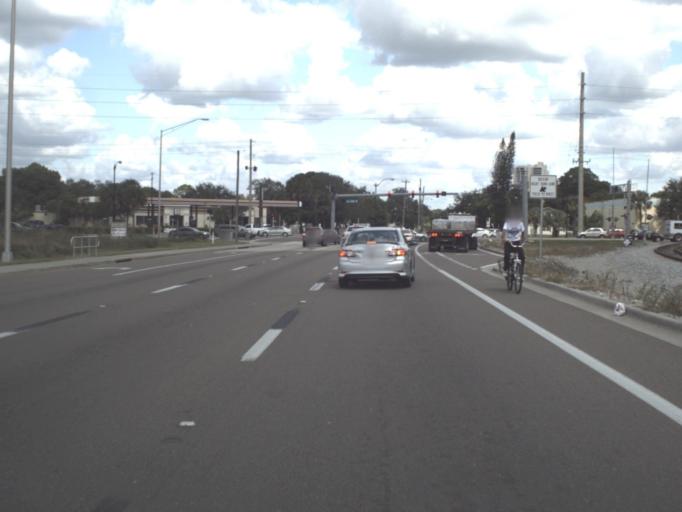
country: US
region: Florida
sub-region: Lee County
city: Fort Myers
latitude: 26.6399
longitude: -81.8606
